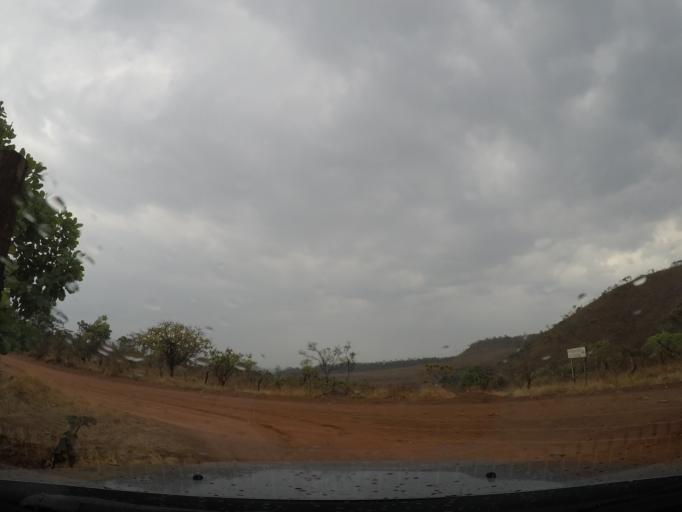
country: BR
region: Goias
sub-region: Pirenopolis
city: Pirenopolis
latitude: -15.8178
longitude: -48.8967
